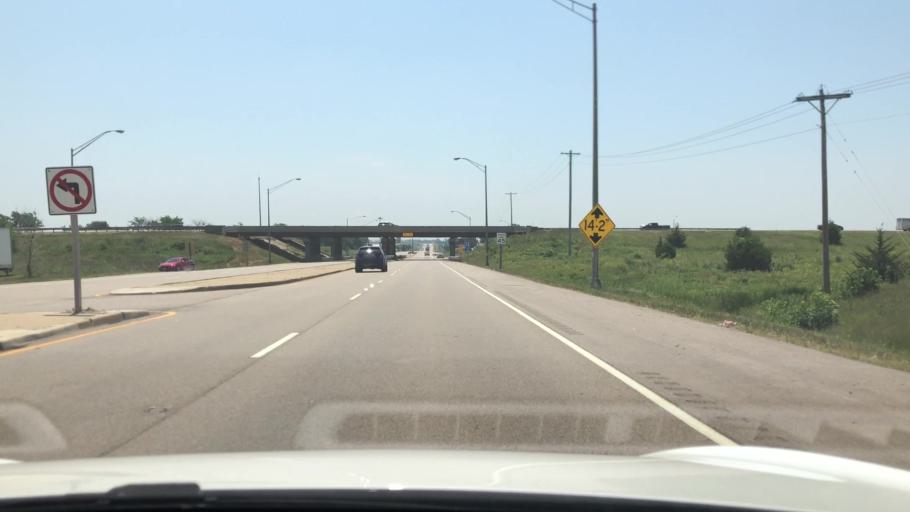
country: US
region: Illinois
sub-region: McLean County
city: Bloomington
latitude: 40.4375
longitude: -88.9906
